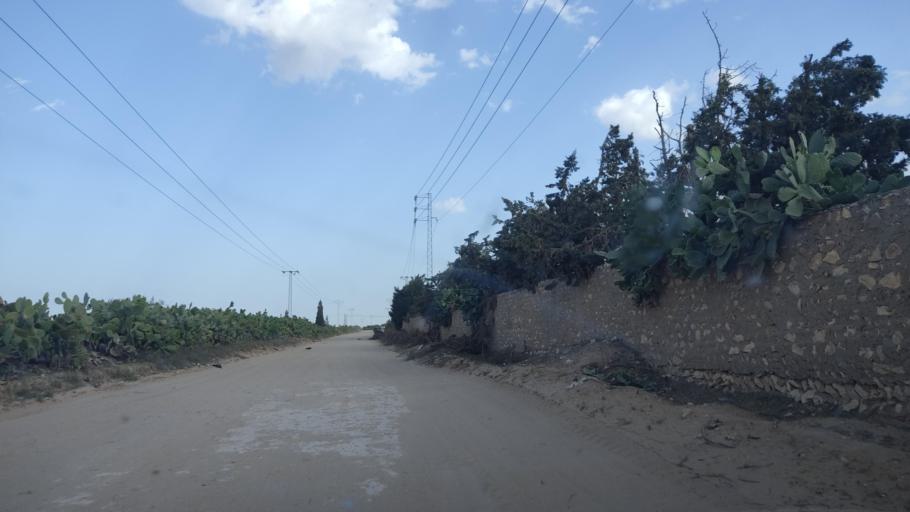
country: TN
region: Safaqis
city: Sfax
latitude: 34.8585
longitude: 10.6028
